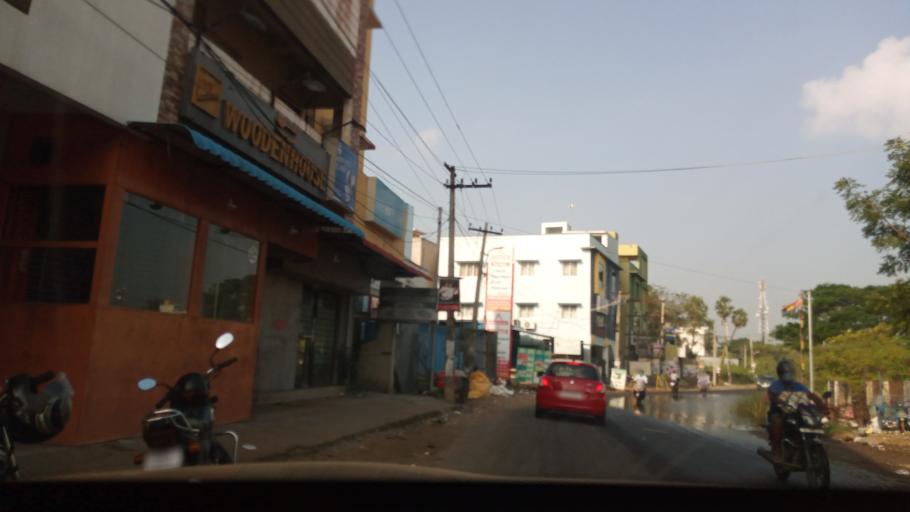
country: IN
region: Tamil Nadu
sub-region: Kancheepuram
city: Vengavasal
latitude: 12.7839
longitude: 80.2229
